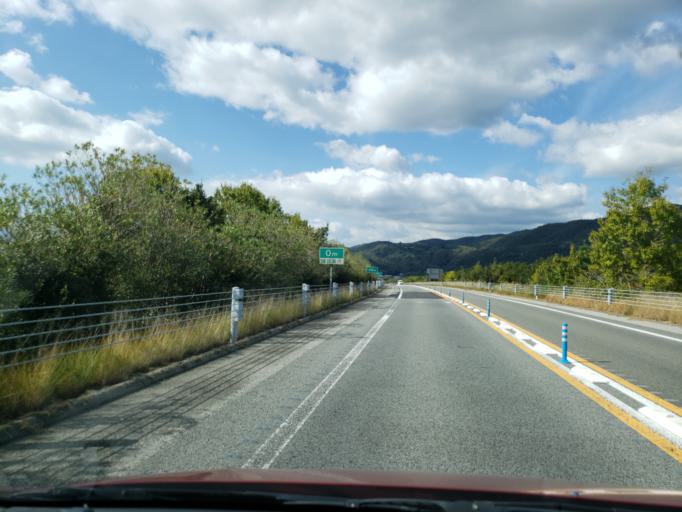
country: JP
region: Tokushima
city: Kamojimacho-jogejima
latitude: 34.1187
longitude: 134.3350
